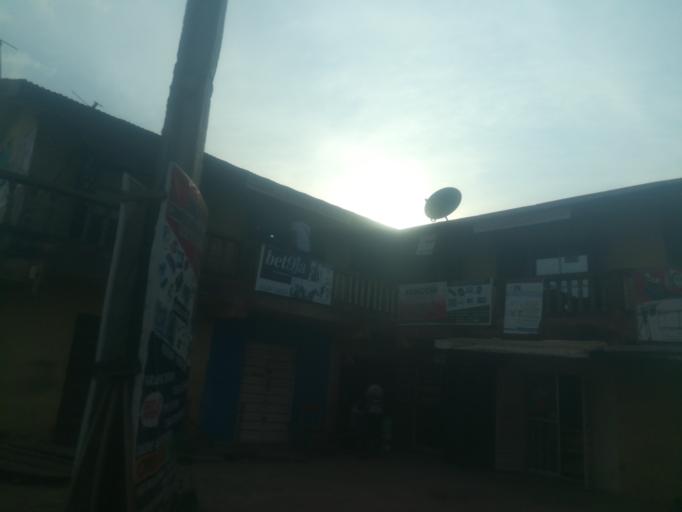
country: NG
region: Ogun
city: Abeokuta
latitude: 7.1595
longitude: 3.3108
